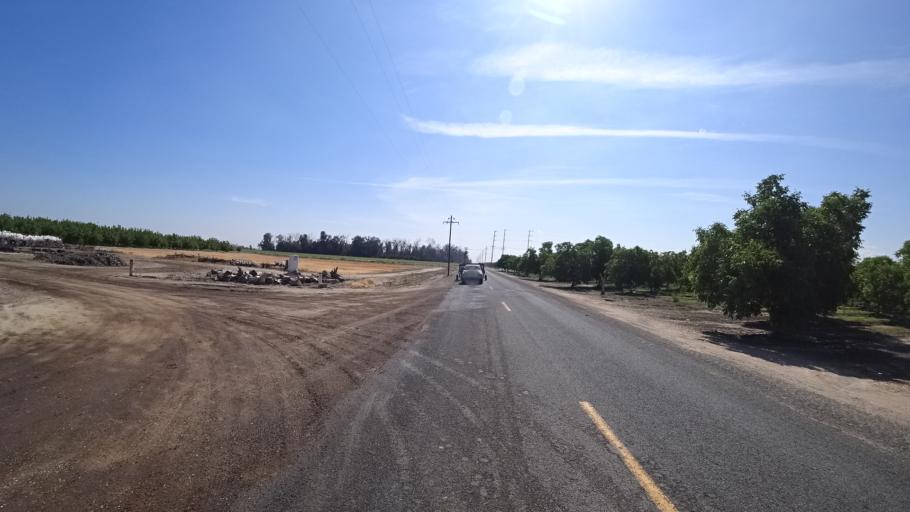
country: US
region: California
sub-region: Kings County
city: Armona
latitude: 36.2548
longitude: -119.6929
